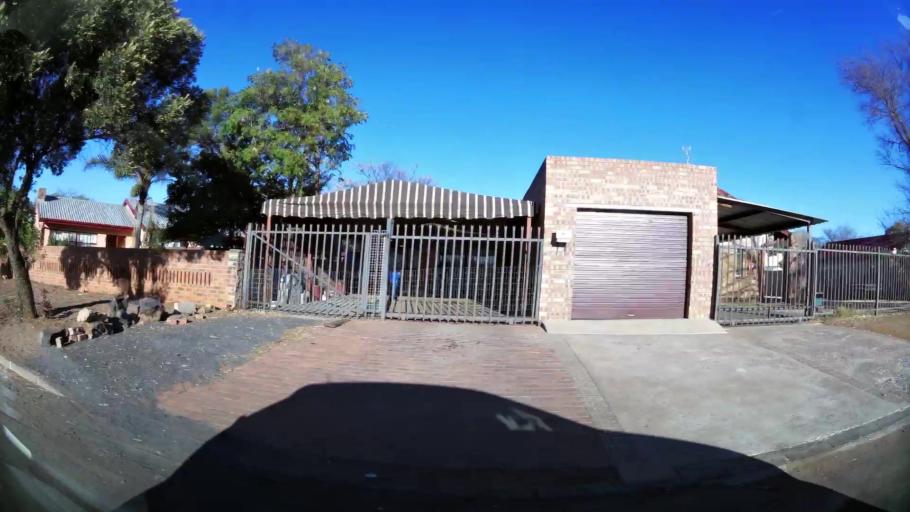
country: ZA
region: Northern Cape
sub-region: Frances Baard District Municipality
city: Kimberley
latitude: -28.7501
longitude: 24.7255
